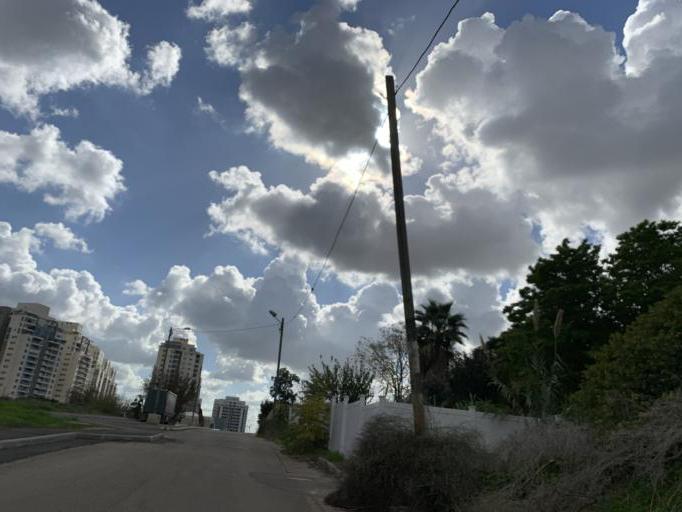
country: IL
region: Central District
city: Kfar Saba
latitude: 32.1697
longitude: 34.8974
